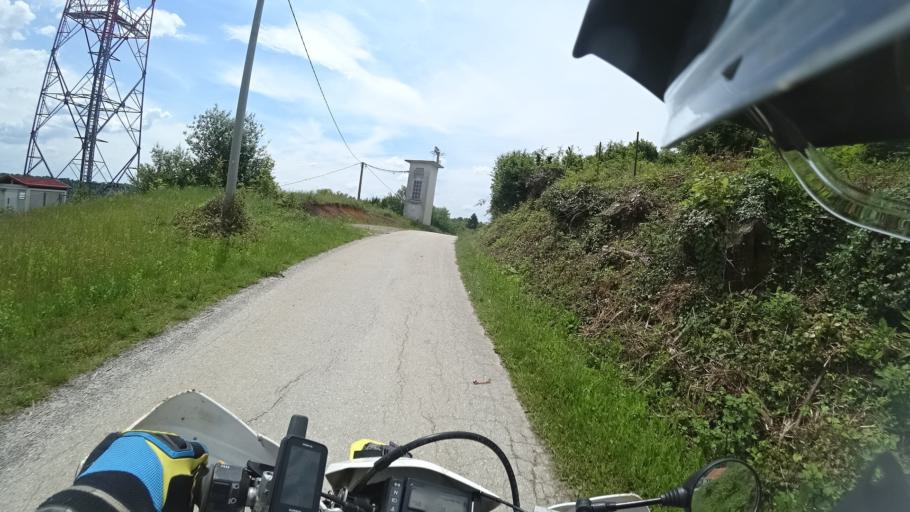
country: HR
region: Karlovacka
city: Vojnic
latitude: 45.2468
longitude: 15.7113
